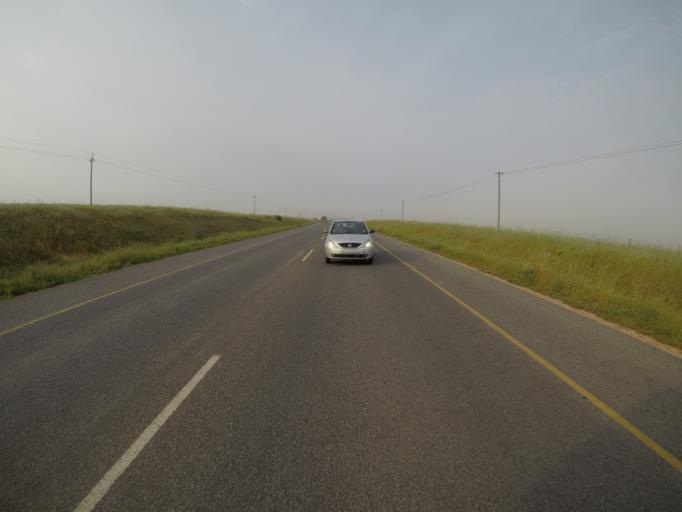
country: ZA
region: Western Cape
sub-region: City of Cape Town
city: Kraaifontein
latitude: -33.6552
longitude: 18.7087
